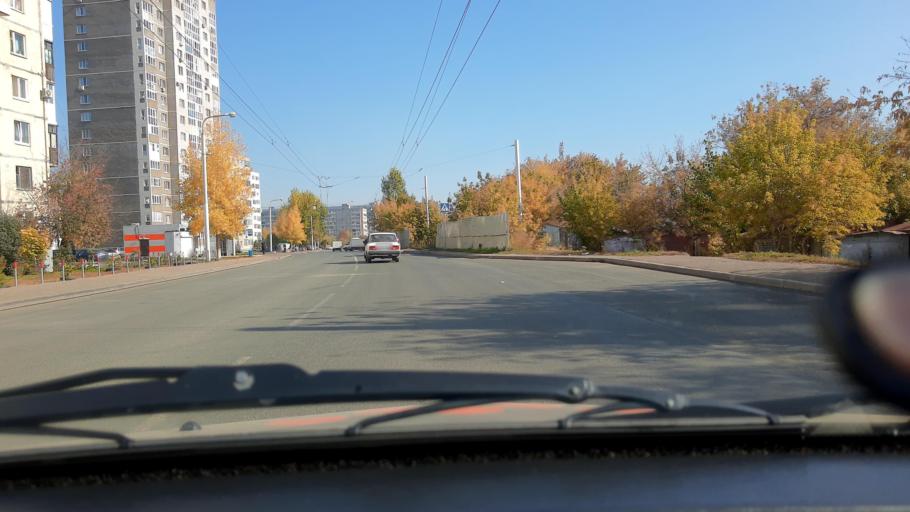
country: RU
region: Bashkortostan
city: Ufa
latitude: 54.7734
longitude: 56.1173
